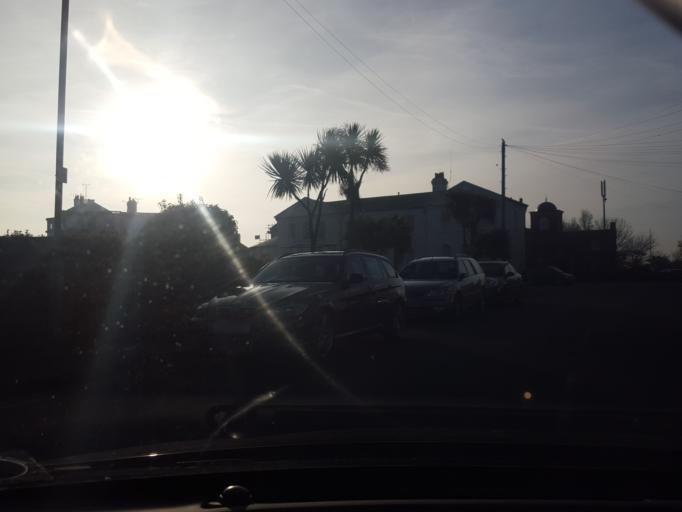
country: GB
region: England
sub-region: Essex
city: Walton-on-the-Naze
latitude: 51.8464
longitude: 1.2695
